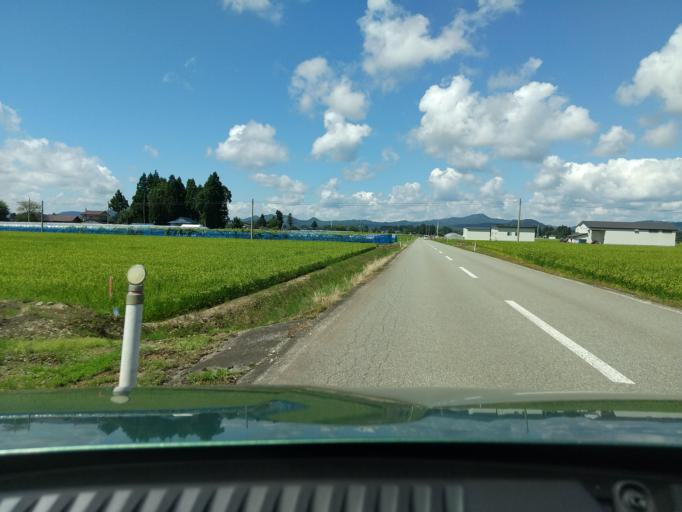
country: JP
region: Akita
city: Kakunodatemachi
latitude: 39.5729
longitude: 140.5926
